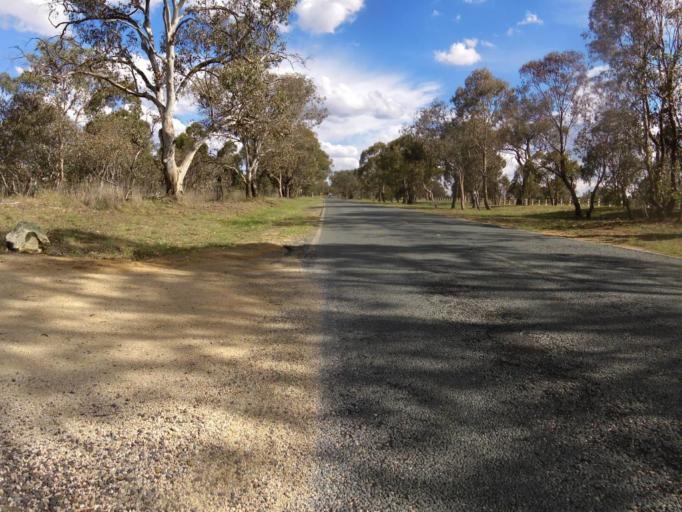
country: AU
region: Australian Capital Territory
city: Belconnen
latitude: -35.1775
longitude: 149.0722
